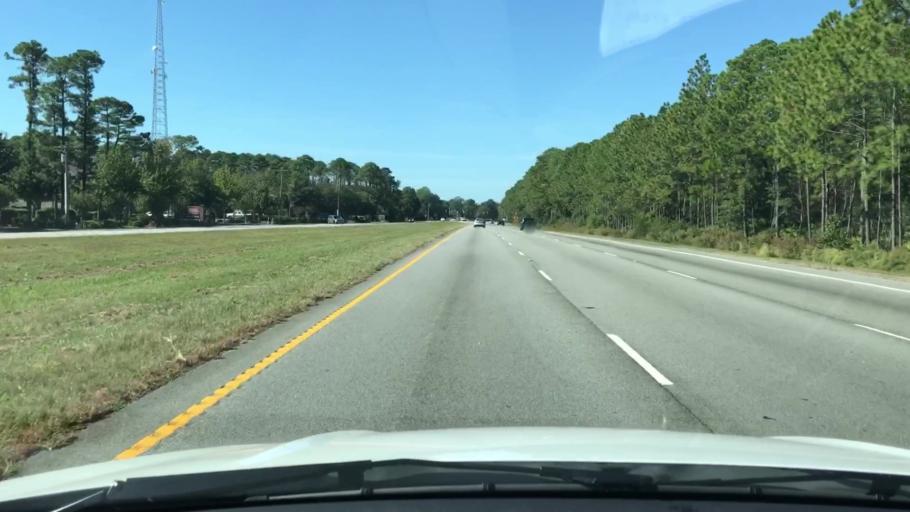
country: US
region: South Carolina
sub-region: Beaufort County
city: Bluffton
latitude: 32.2497
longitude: -80.8374
